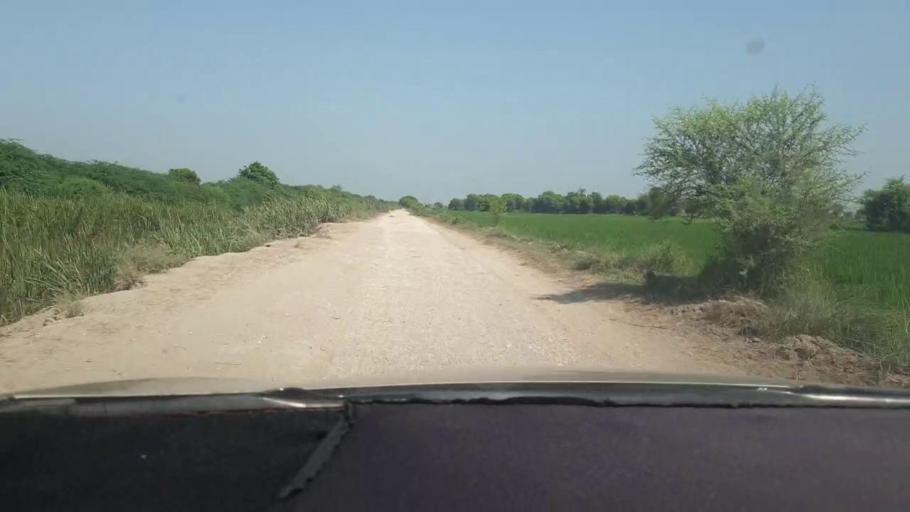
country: PK
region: Sindh
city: Miro Khan
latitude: 27.7040
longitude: 68.0815
